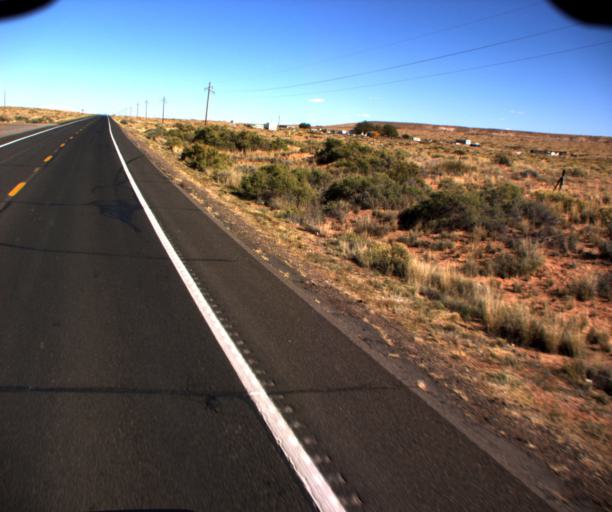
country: US
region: Arizona
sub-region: Coconino County
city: Tuba City
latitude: 36.1301
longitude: -111.1903
